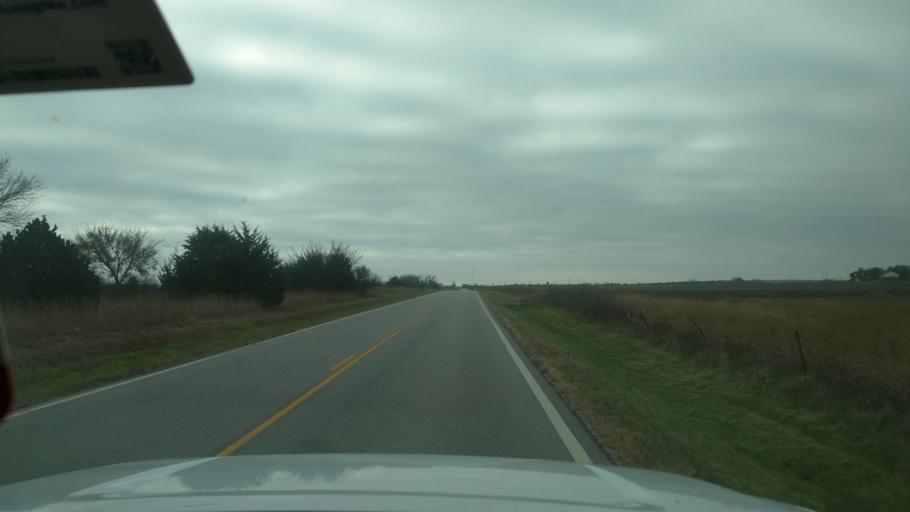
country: US
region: Kansas
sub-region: Greenwood County
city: Eureka
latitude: 37.6555
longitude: -96.2346
